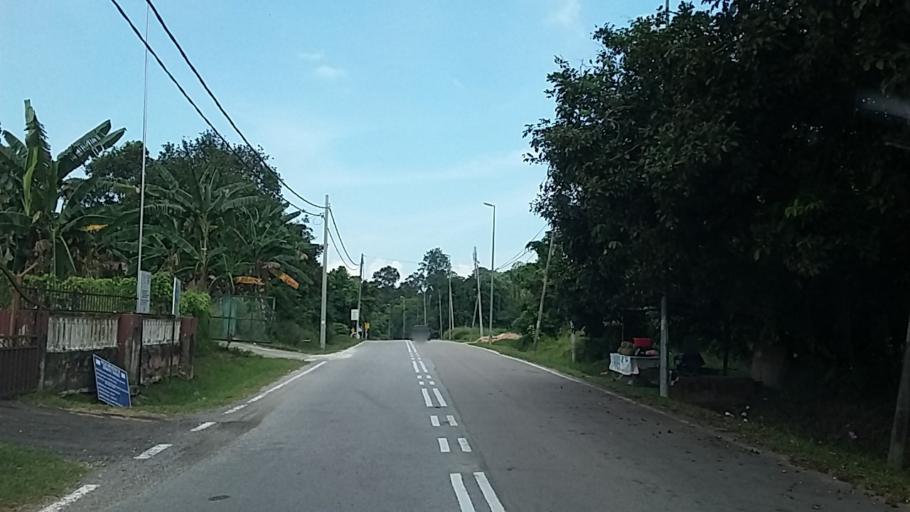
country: MY
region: Johor
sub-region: Daerah Batu Pahat
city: Batu Pahat
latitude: 1.7926
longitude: 102.8955
